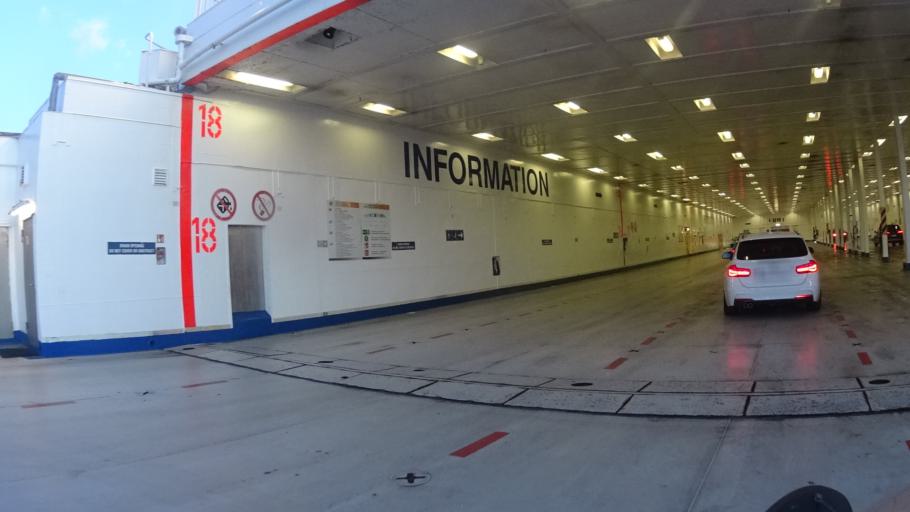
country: SE
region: Skane
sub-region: Trelleborgs Kommun
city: Trelleborg
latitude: 55.3674
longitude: 13.1563
